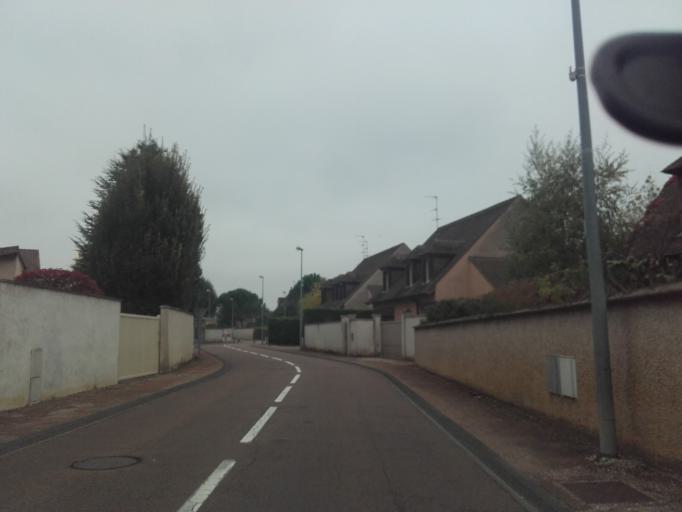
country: FR
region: Bourgogne
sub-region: Departement de la Cote-d'Or
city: Beaune
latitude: 47.0287
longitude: 4.8319
